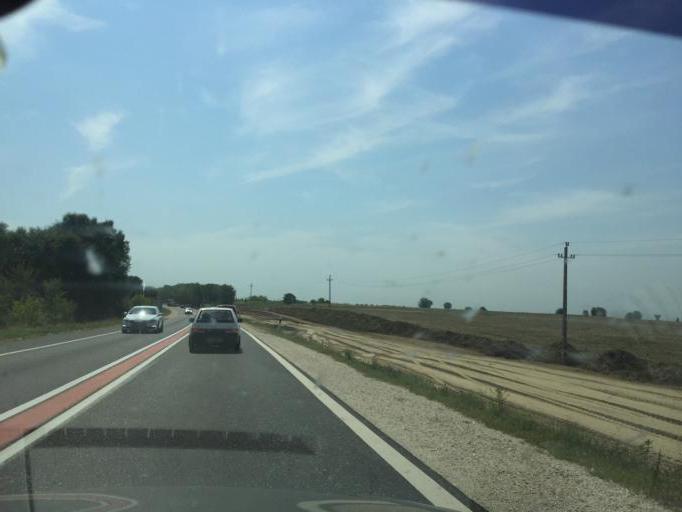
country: HU
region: Pest
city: Dunakeszi
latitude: 47.6492
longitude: 19.1603
